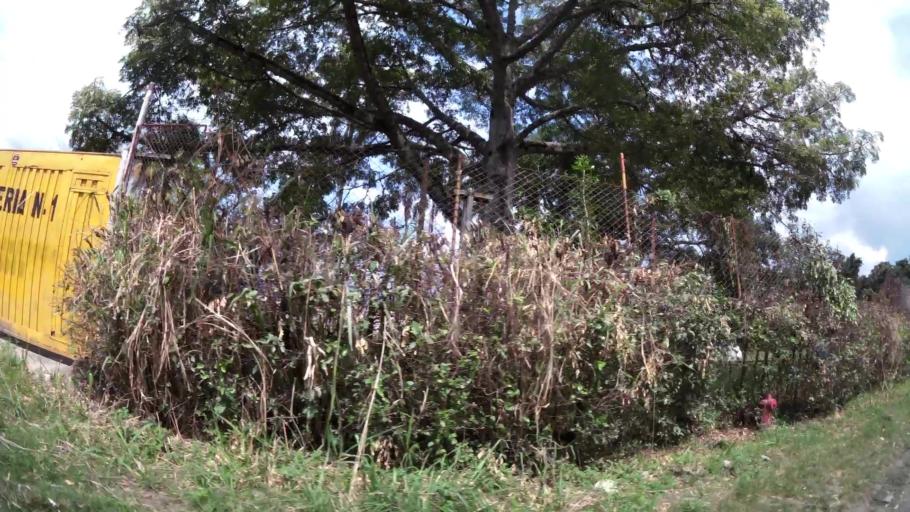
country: CO
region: Valle del Cauca
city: Cali
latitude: 3.4943
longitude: -76.4720
